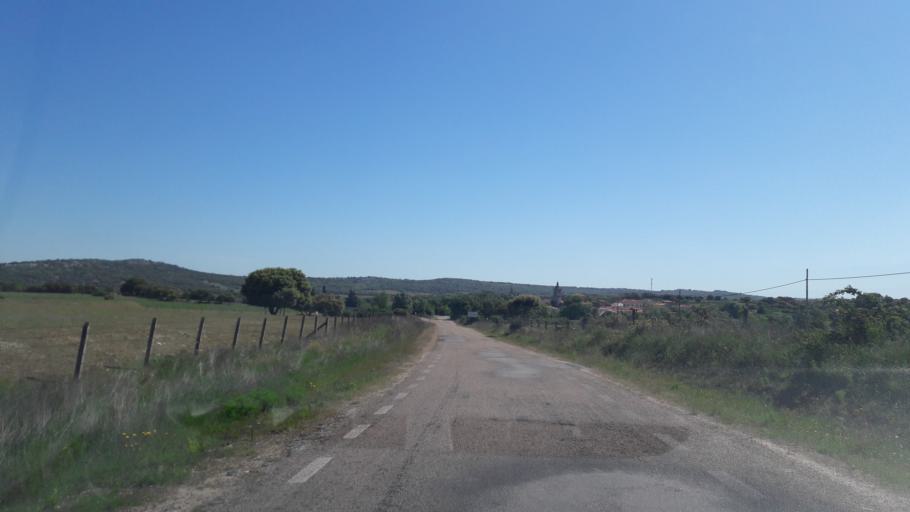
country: ES
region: Castille and Leon
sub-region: Provincia de Salamanca
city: Olmedo de Camaces
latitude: 40.8764
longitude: -6.6307
